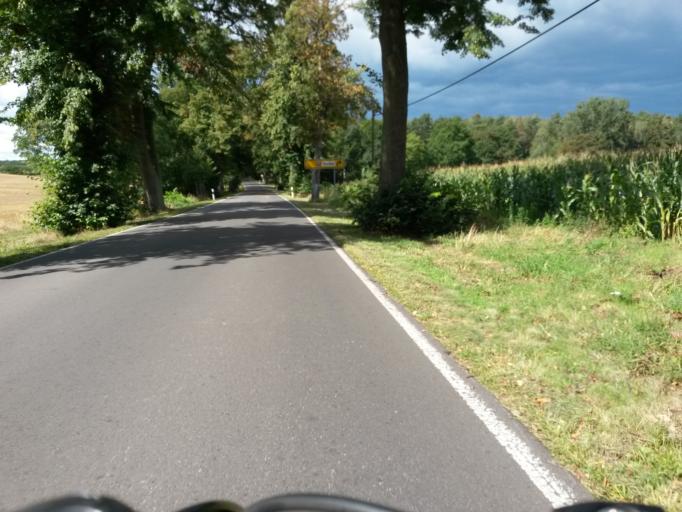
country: DE
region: Brandenburg
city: Angermunde
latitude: 53.0100
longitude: 13.9607
